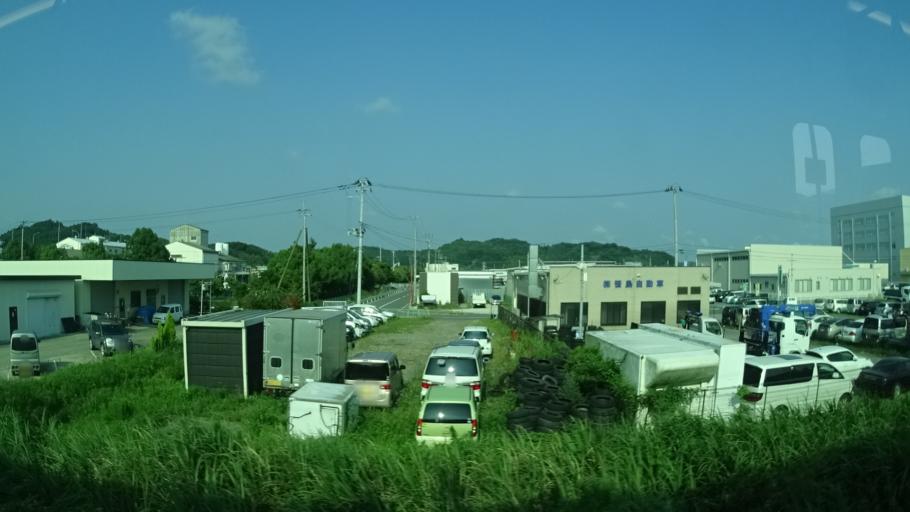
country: JP
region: Fukushima
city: Iwaki
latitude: 36.9854
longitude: 140.8629
